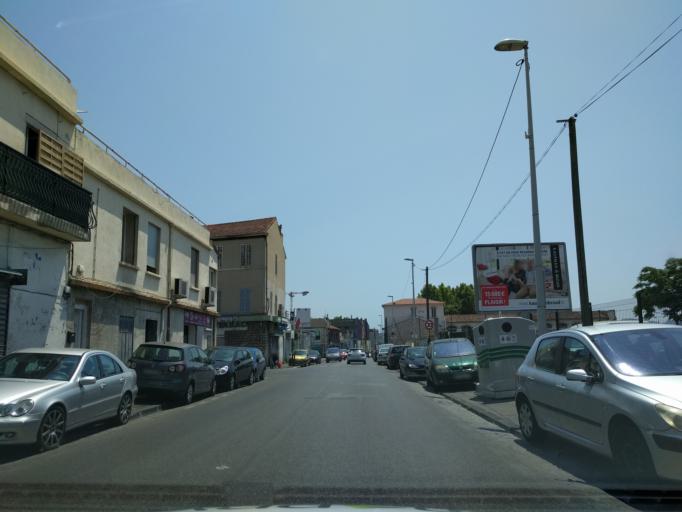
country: FR
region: Provence-Alpes-Cote d'Azur
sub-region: Departement des Bouches-du-Rhone
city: Marseille 14
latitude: 43.3281
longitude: 5.3597
